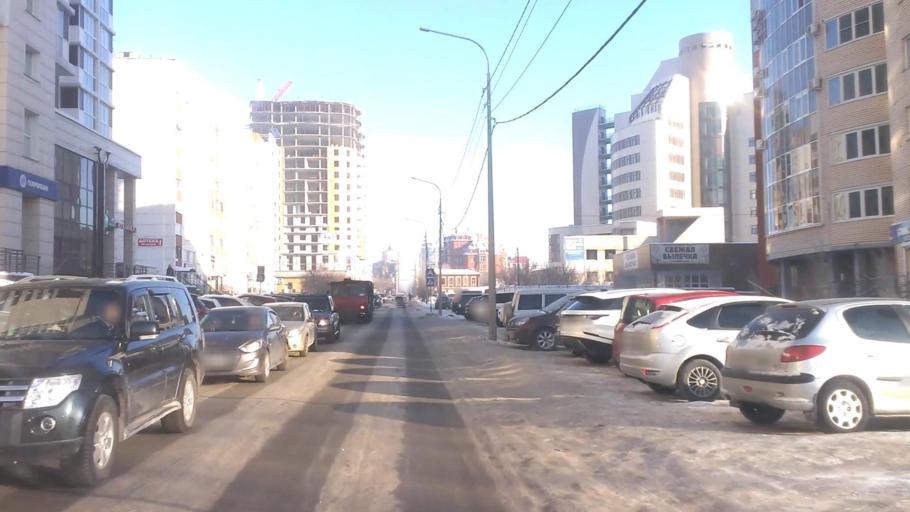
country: RU
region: Altai Krai
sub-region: Gorod Barnaulskiy
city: Barnaul
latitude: 53.3372
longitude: 83.7787
